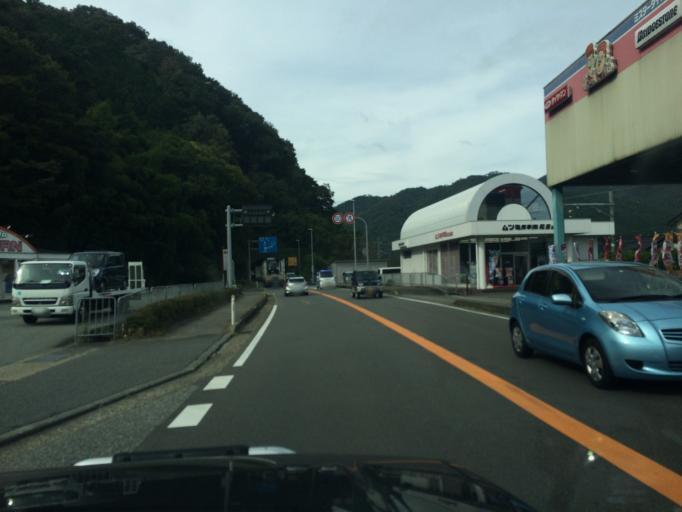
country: JP
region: Hyogo
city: Toyooka
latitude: 35.3513
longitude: 134.8352
